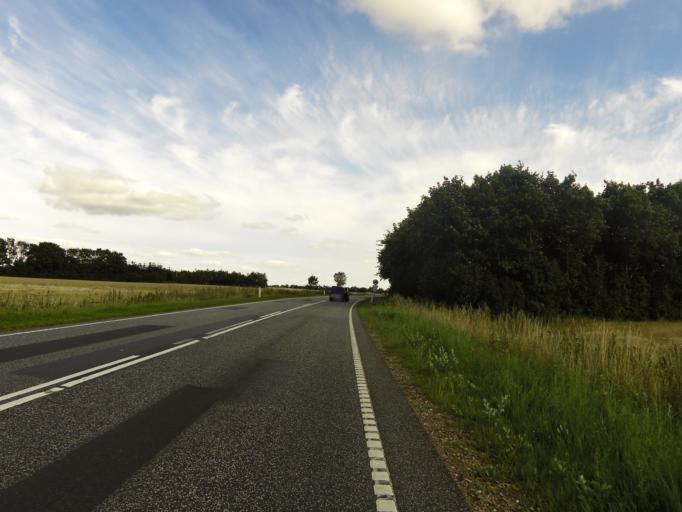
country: DK
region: South Denmark
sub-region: Tonder Kommune
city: Toftlund
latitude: 55.2136
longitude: 9.0375
